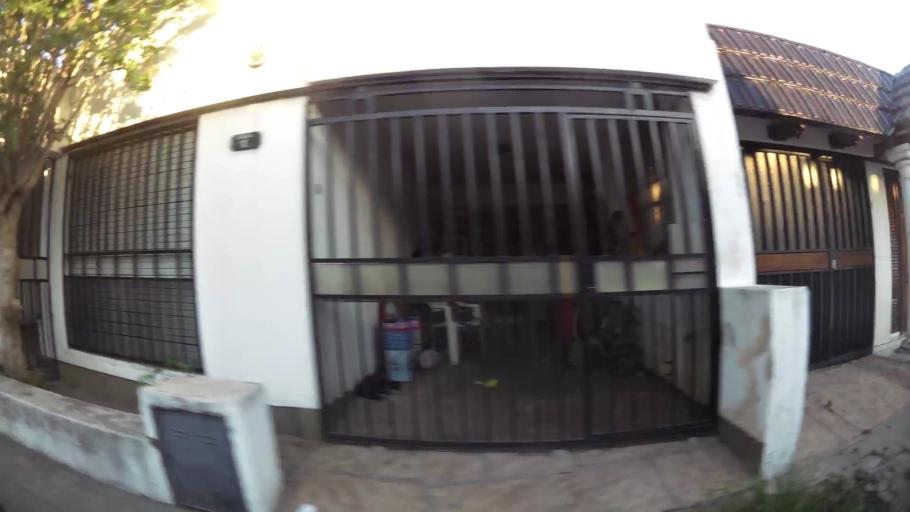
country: AR
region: Cordoba
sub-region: Departamento de Capital
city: Cordoba
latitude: -31.3795
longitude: -64.2115
